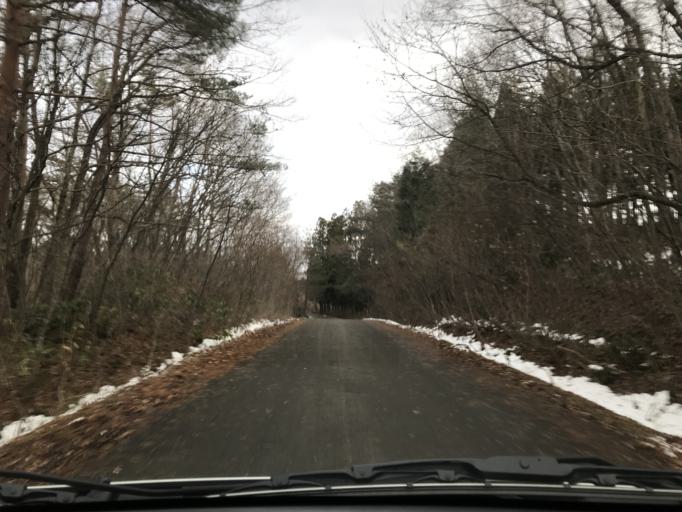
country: JP
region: Iwate
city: Ichinoseki
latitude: 38.9876
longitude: 141.0031
